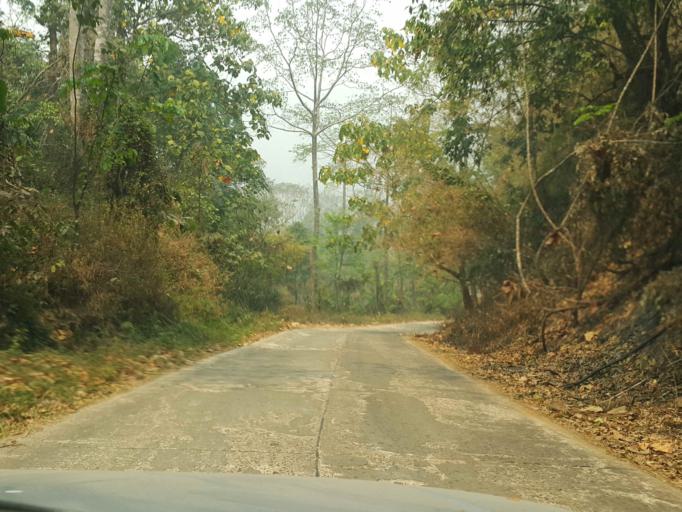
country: TH
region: Chiang Mai
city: Mae Taeng
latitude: 19.2098
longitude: 98.8745
